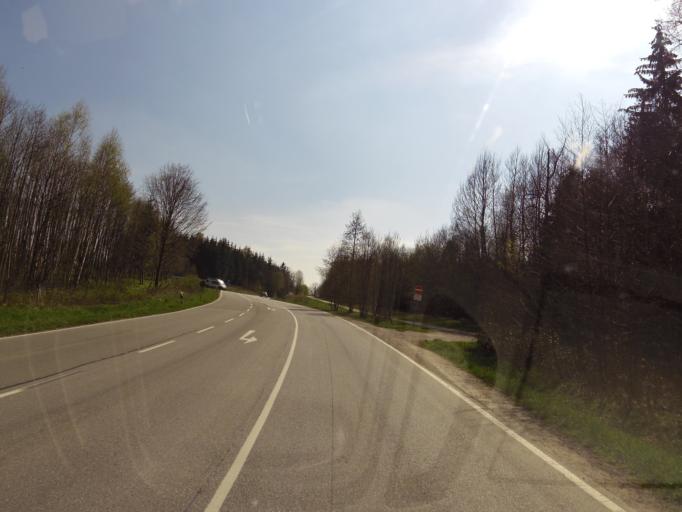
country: DE
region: Bavaria
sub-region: Upper Bavaria
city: Sulzemoos
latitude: 48.2795
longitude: 11.2695
